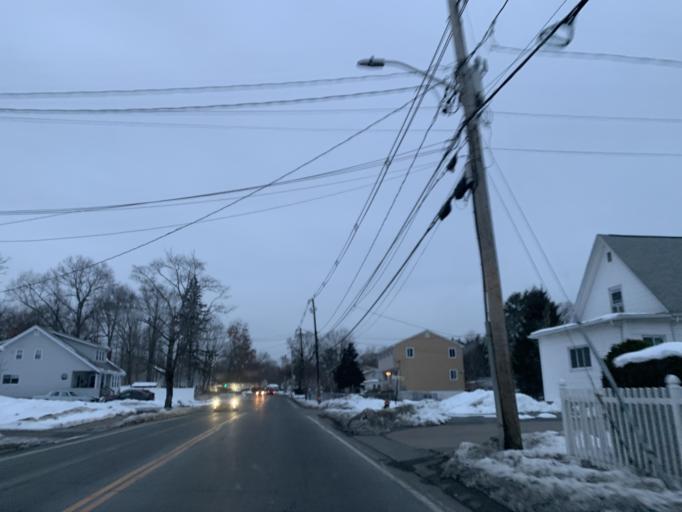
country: US
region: Massachusetts
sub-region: Norfolk County
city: Stoughton
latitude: 42.1344
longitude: -71.1105
